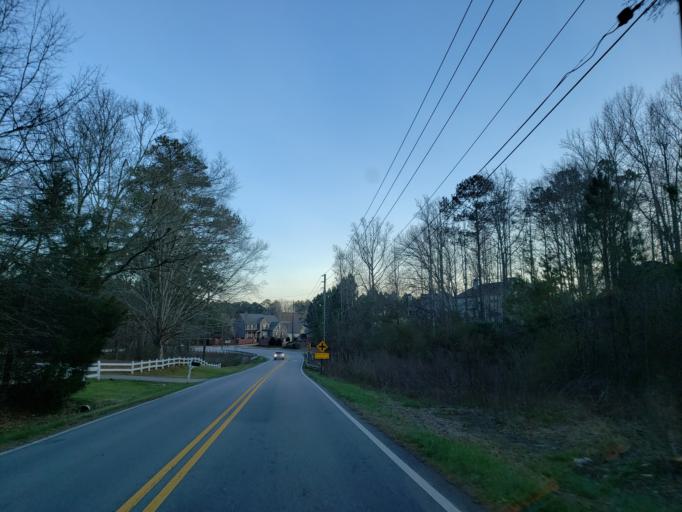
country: US
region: Georgia
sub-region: Cobb County
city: Acworth
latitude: 34.0017
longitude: -84.7375
